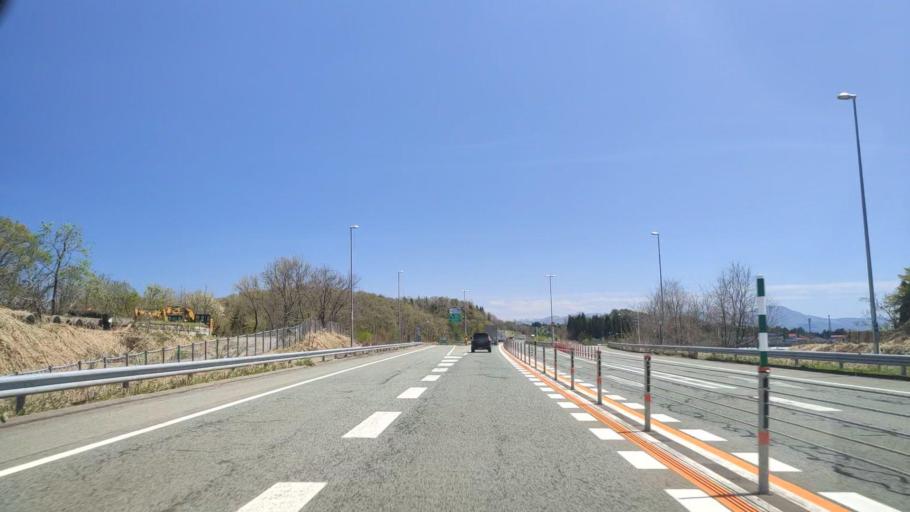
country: JP
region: Yamagata
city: Obanazawa
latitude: 38.6608
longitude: 140.3615
